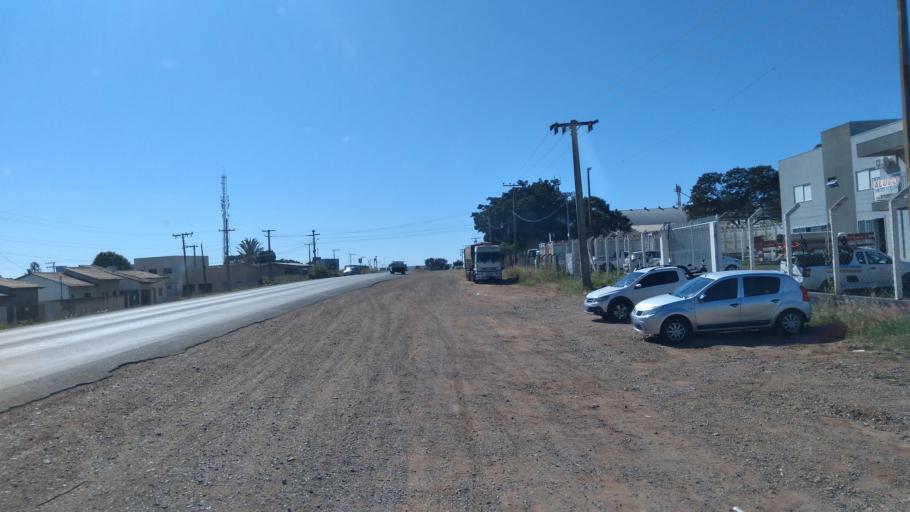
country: BR
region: Goias
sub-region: Mineiros
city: Mineiros
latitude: -17.5832
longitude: -52.5485
